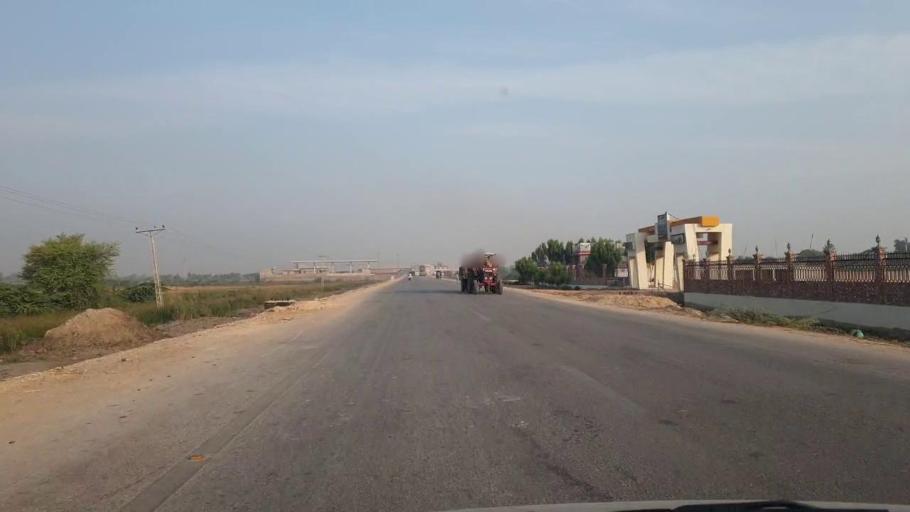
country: PK
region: Sindh
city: Badin
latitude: 24.6817
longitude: 68.8253
